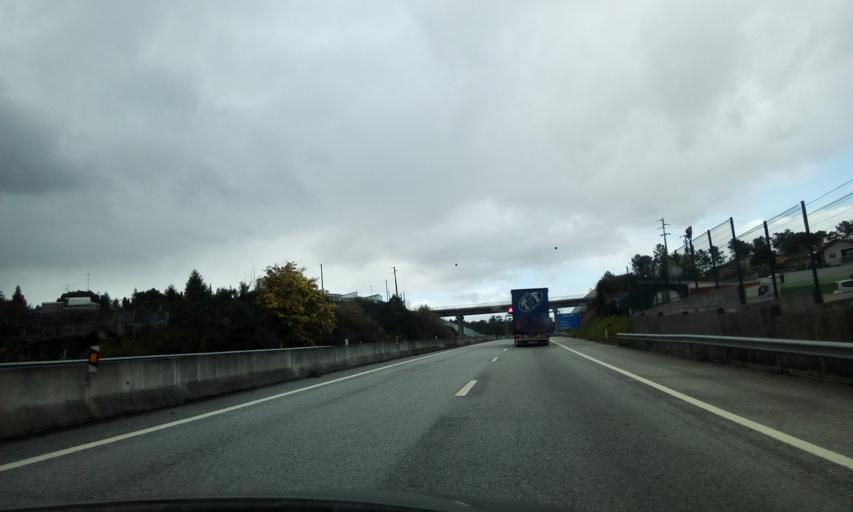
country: PT
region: Viseu
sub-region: Viseu
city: Rio de Loba
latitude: 40.6405
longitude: -7.8555
